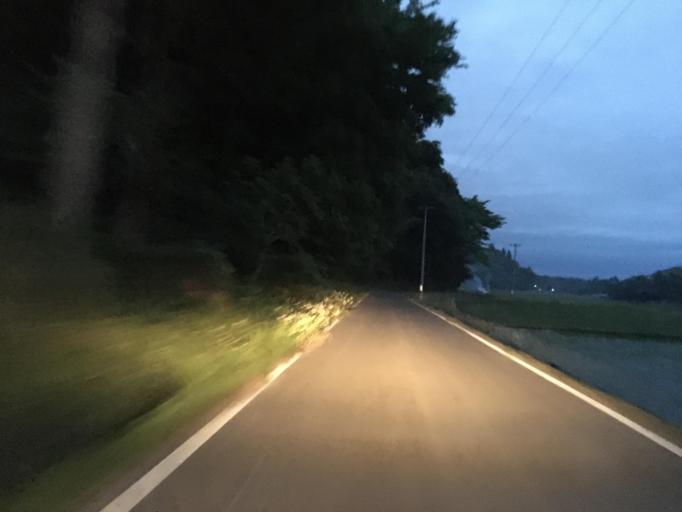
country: JP
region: Miyagi
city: Furukawa
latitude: 38.7853
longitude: 140.9250
